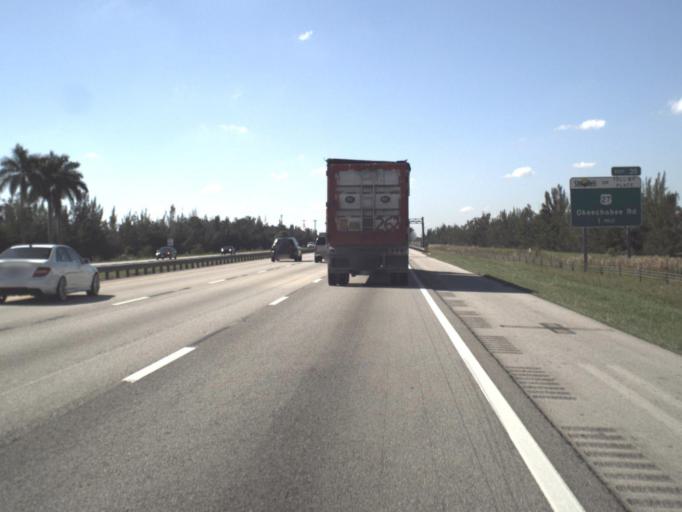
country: US
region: Florida
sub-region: Miami-Dade County
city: Palm Springs North
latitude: 25.9215
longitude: -80.3779
